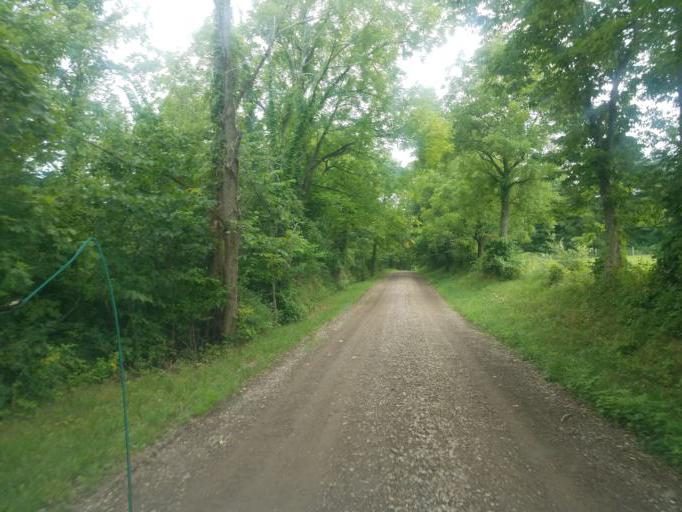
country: US
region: Ohio
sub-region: Knox County
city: Oak Hill
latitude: 40.3298
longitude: -82.1299
